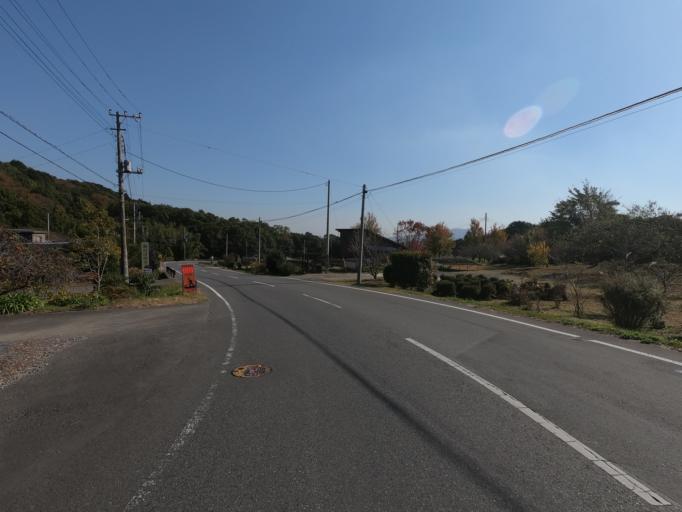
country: JP
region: Ibaraki
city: Tsukuba
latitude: 36.2299
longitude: 140.1395
